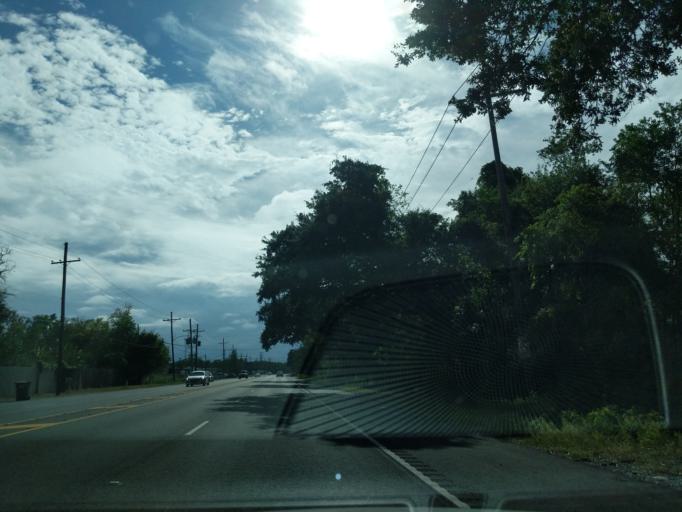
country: US
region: Louisiana
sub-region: Saint Bernard Parish
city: Chalmette
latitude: 30.0443
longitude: -89.8930
